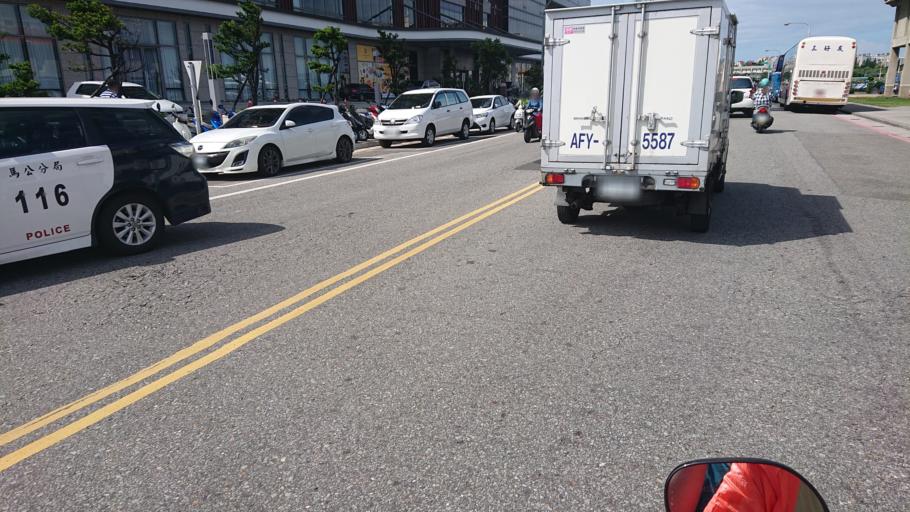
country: TW
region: Taiwan
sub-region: Penghu
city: Ma-kung
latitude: 23.5665
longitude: 119.5721
